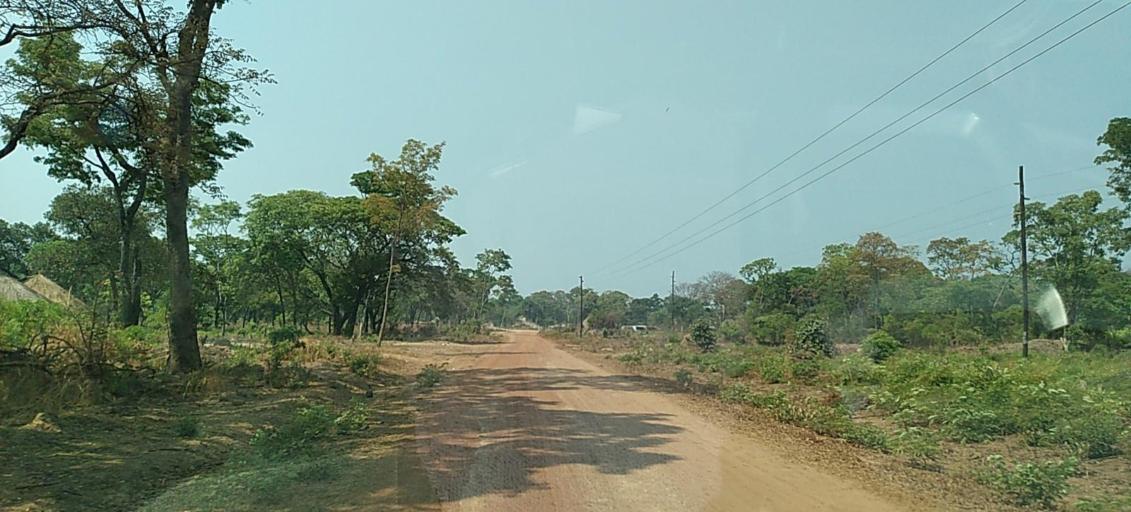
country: ZM
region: Copperbelt
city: Kalulushi
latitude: -13.1057
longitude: 27.4027
